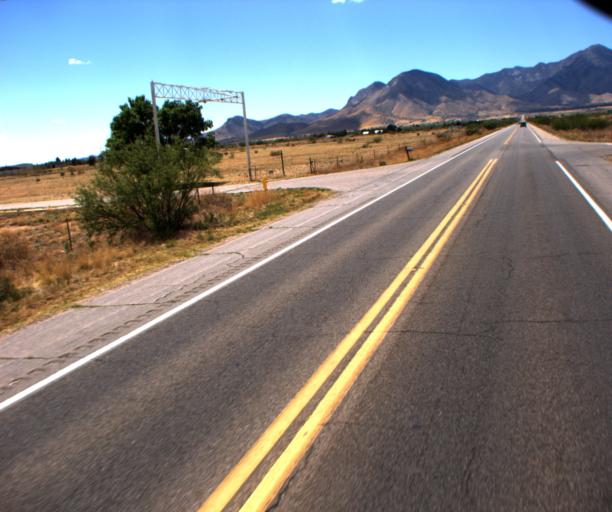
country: US
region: Arizona
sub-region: Cochise County
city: Sierra Vista Southeast
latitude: 31.3800
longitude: -110.1555
